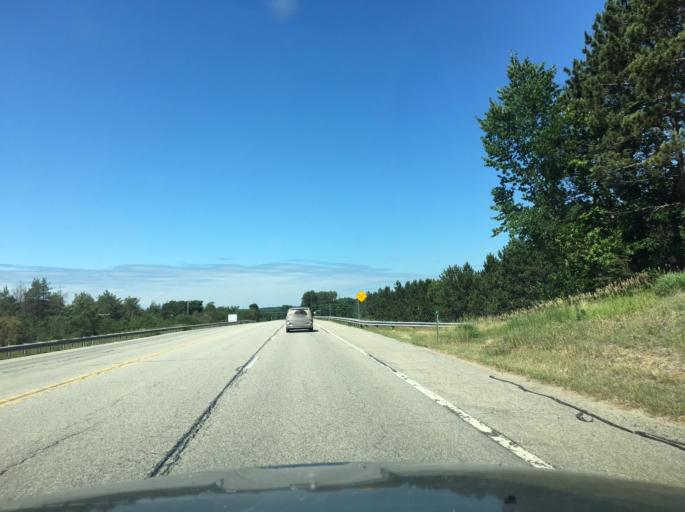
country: US
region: Michigan
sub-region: Osceola County
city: Reed City
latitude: 43.8878
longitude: -85.6166
